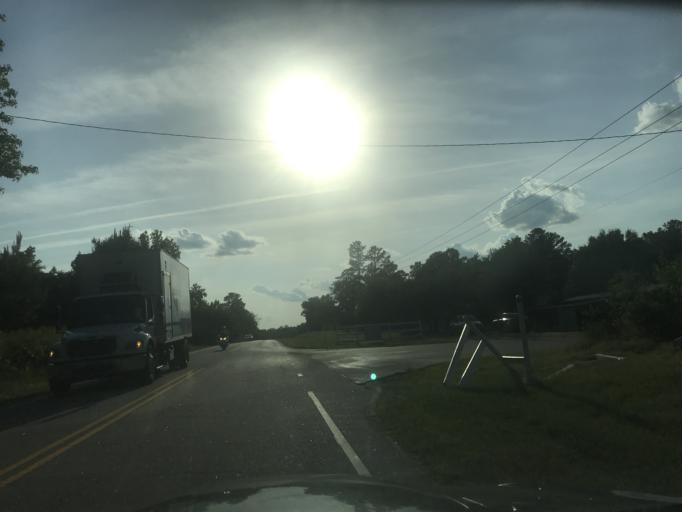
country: US
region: North Carolina
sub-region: Wake County
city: Knightdale
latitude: 35.7545
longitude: -78.5247
